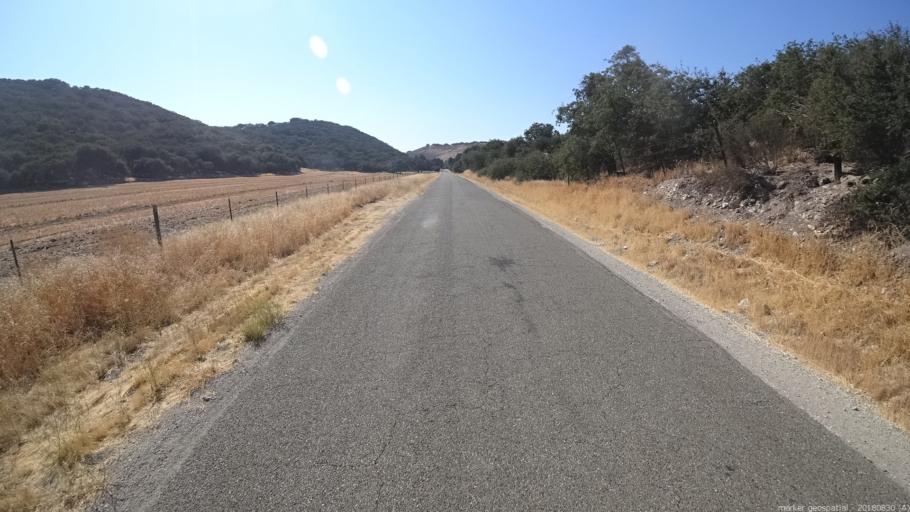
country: US
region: California
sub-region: Monterey County
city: King City
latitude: 36.1140
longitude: -121.1102
